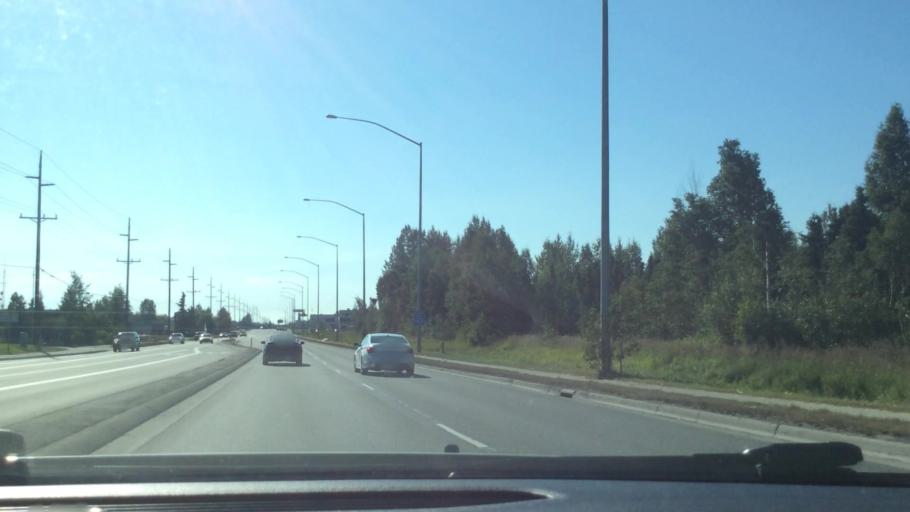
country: US
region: Alaska
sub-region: Anchorage Municipality
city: Anchorage
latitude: 61.1664
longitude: -149.8401
